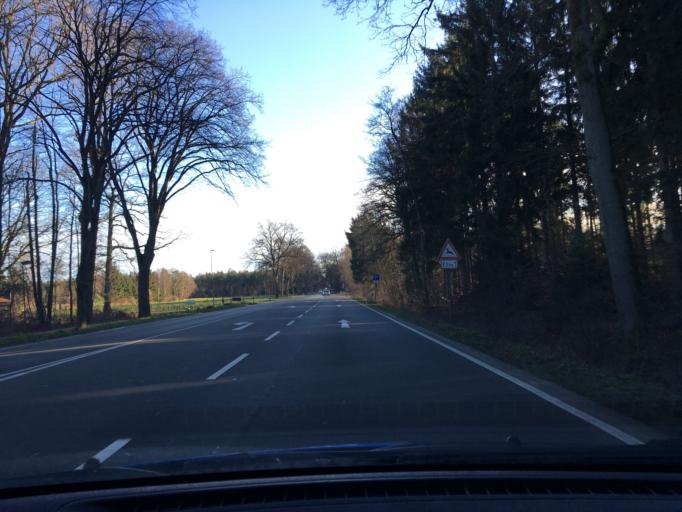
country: DE
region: Lower Saxony
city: Deutsch Evern
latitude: 53.1693
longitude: 10.4281
